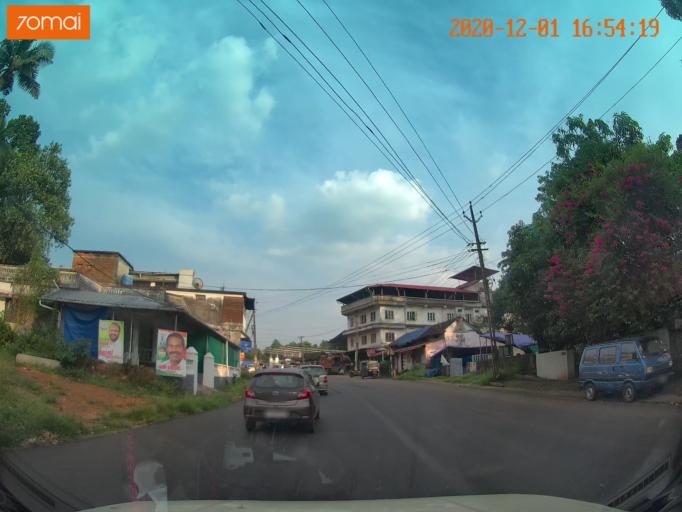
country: IN
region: Kerala
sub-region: Ernakulam
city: Muvattupula
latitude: 9.9724
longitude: 76.6036
